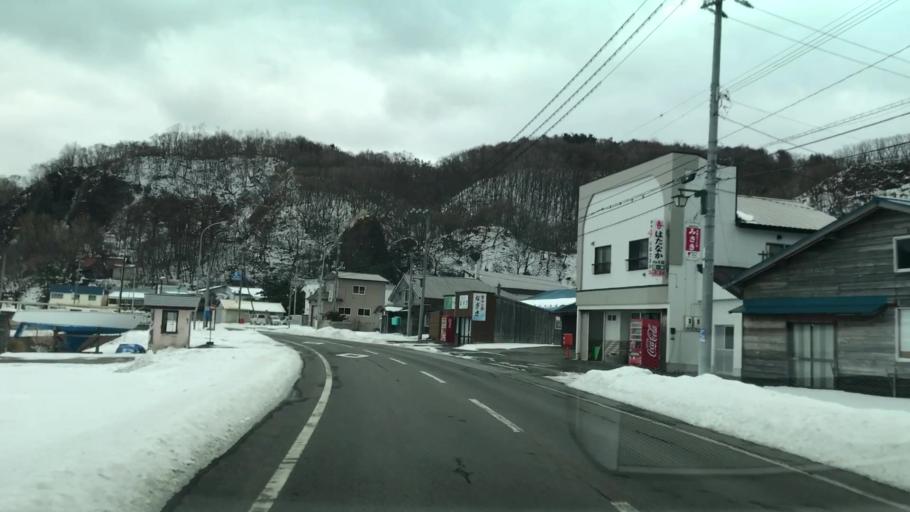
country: JP
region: Hokkaido
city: Iwanai
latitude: 43.3302
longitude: 140.3956
